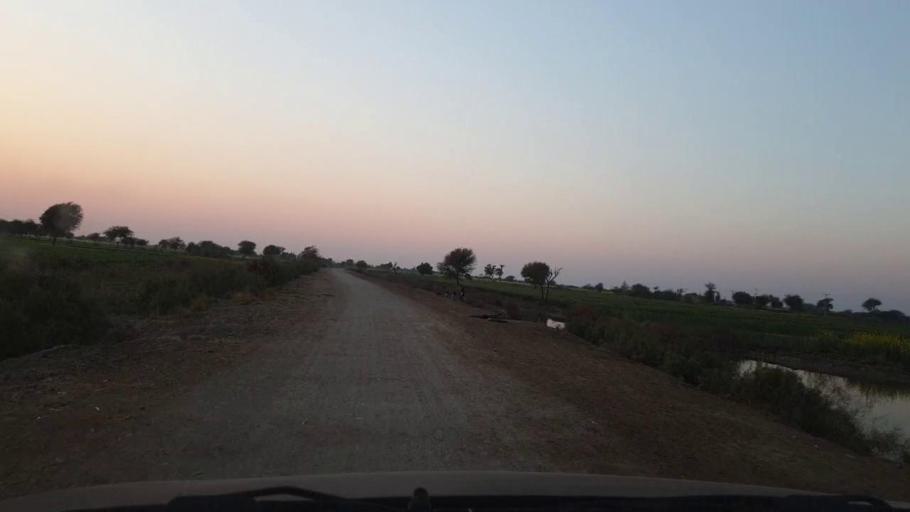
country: PK
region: Sindh
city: Jhol
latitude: 25.9383
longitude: 68.9571
